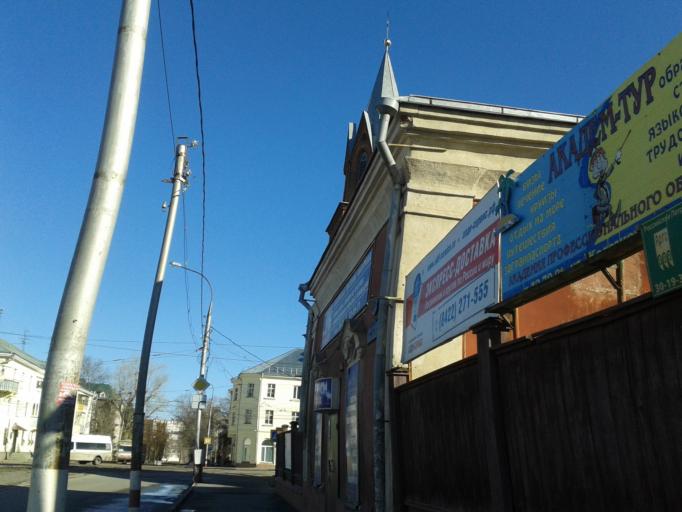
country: RU
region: Ulyanovsk
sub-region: Ulyanovskiy Rayon
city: Ulyanovsk
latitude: 54.3125
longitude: 48.3874
